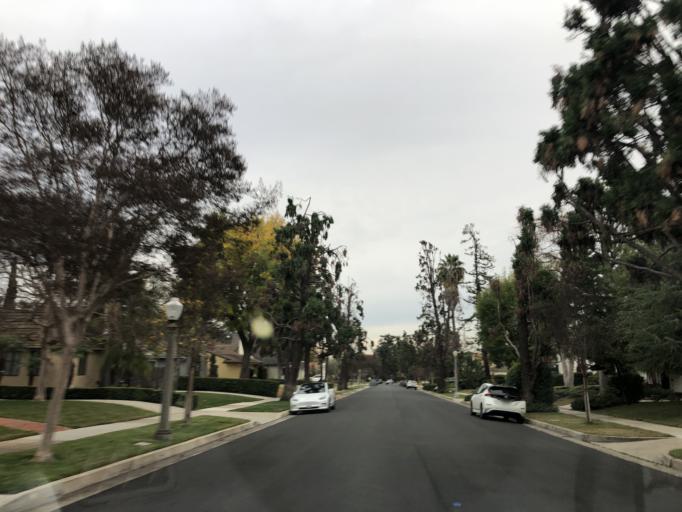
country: US
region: California
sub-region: Los Angeles County
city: San Marino
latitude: 34.1232
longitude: -118.0986
